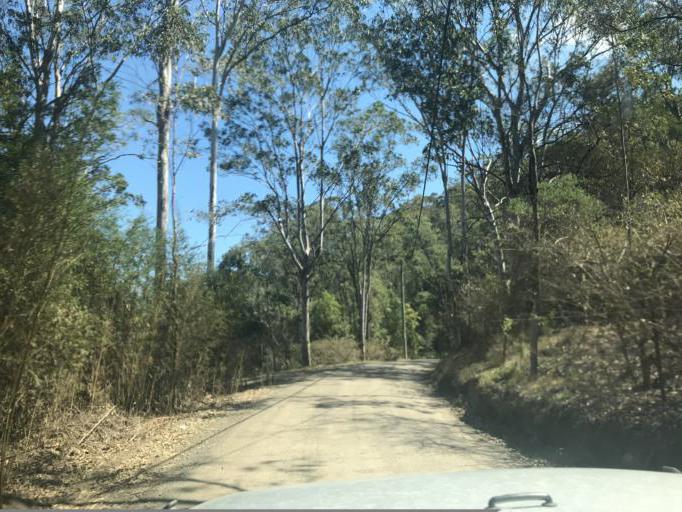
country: AU
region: New South Wales
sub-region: Hawkesbury
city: Pitt Town
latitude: -33.4173
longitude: 150.9099
